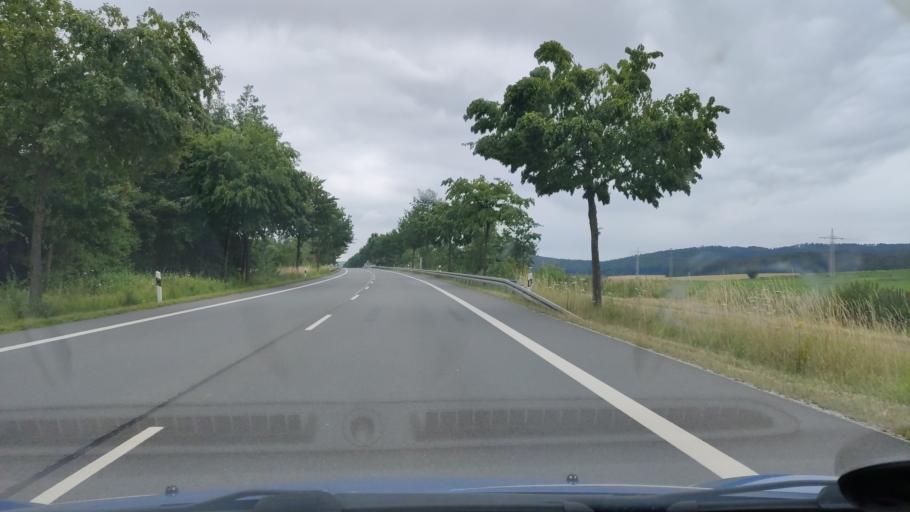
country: DE
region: Lower Saxony
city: Dielmissen
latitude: 51.9628
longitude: 9.6016
